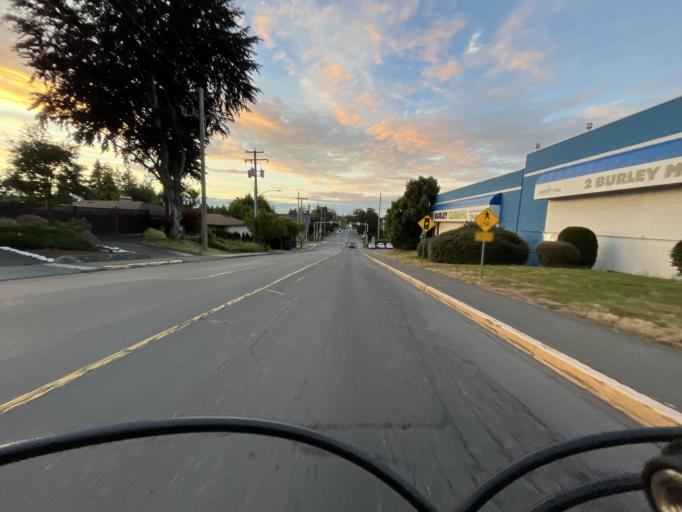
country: CA
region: British Columbia
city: Victoria
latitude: 48.4361
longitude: -123.4028
